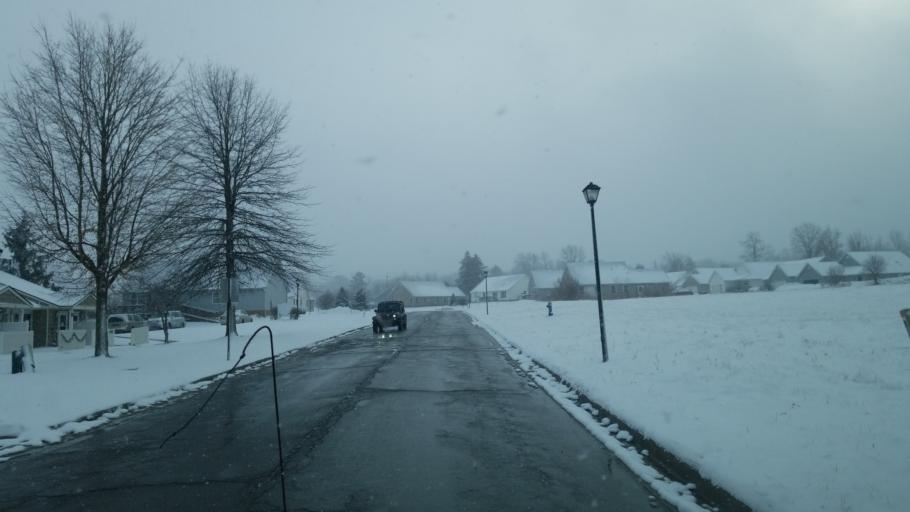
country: US
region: Ohio
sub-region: Geauga County
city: Middlefield
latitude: 41.4665
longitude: -81.0888
